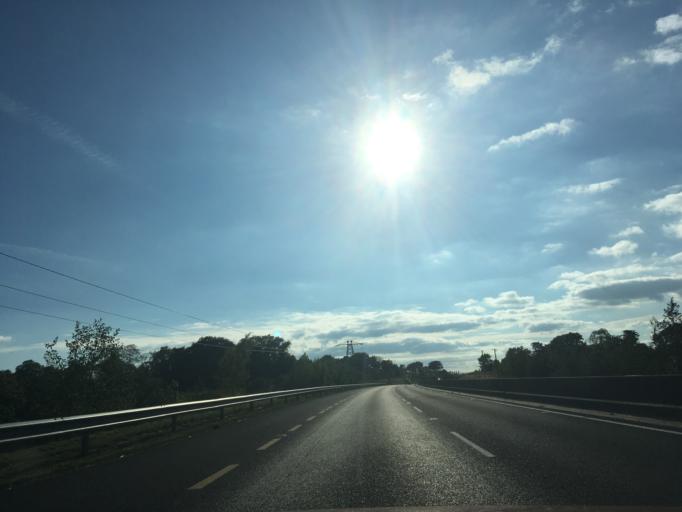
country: IE
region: Munster
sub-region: Waterford
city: Waterford
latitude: 52.2880
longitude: -7.0888
